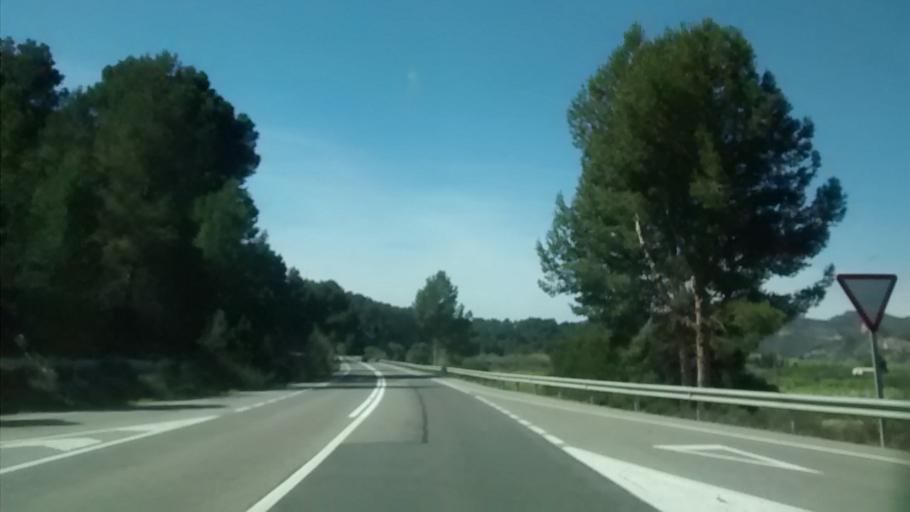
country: ES
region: Catalonia
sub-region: Provincia de Tarragona
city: Ginestar
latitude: 41.0360
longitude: 0.6283
